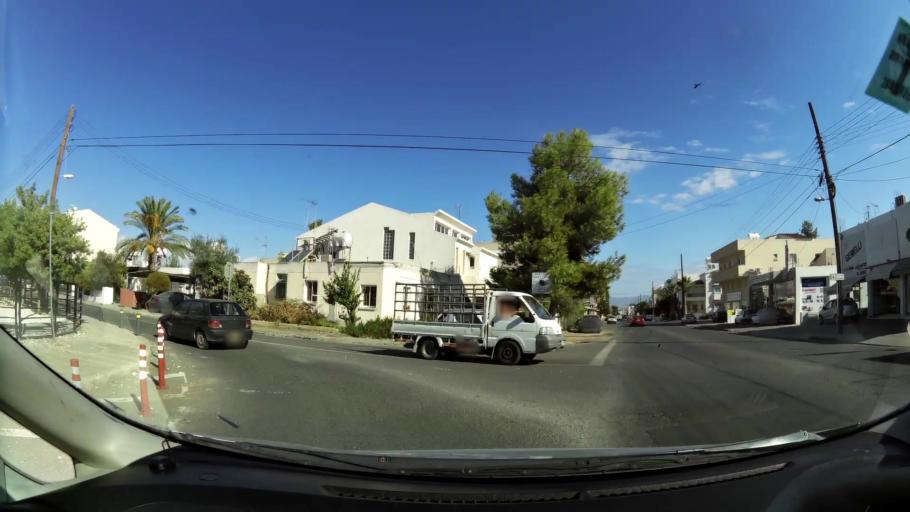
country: CY
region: Lefkosia
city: Tseri
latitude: 35.1237
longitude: 33.3360
